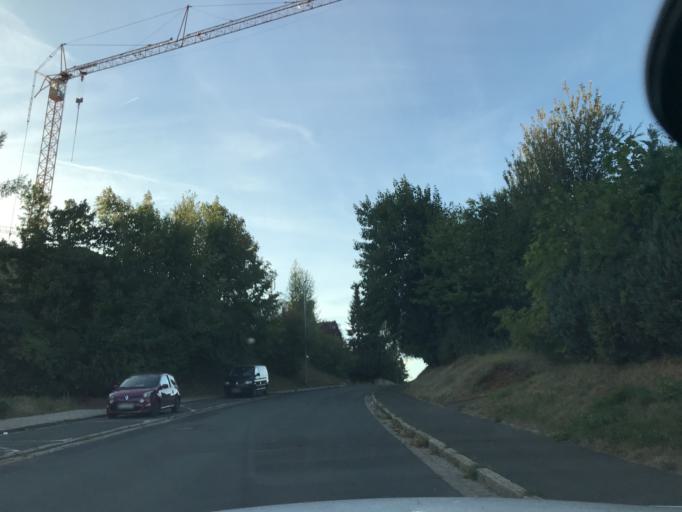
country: DE
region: Bavaria
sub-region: Upper Franconia
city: Pegnitz
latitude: 49.7453
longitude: 11.5414
